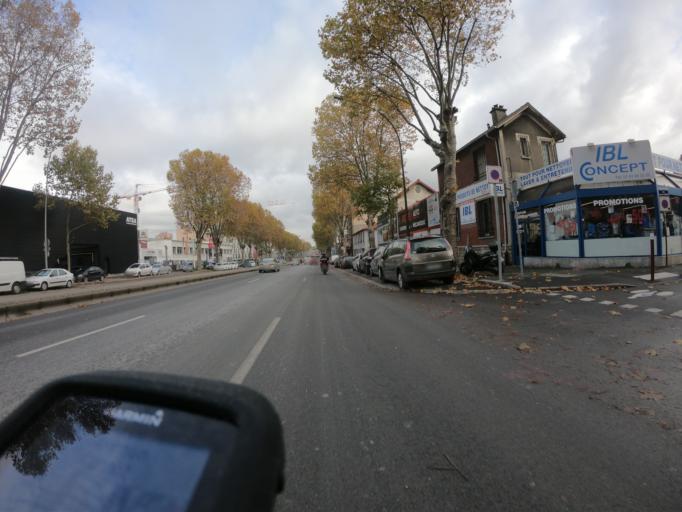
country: FR
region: Ile-de-France
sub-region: Departement du Val-de-Marne
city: Arcueil
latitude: 48.7972
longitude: 2.3223
